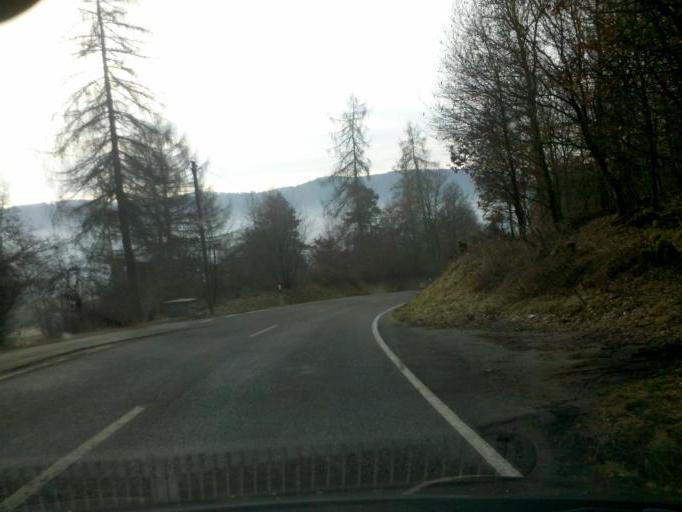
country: DE
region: Hesse
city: Dillenburg
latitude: 50.7822
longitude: 8.2895
